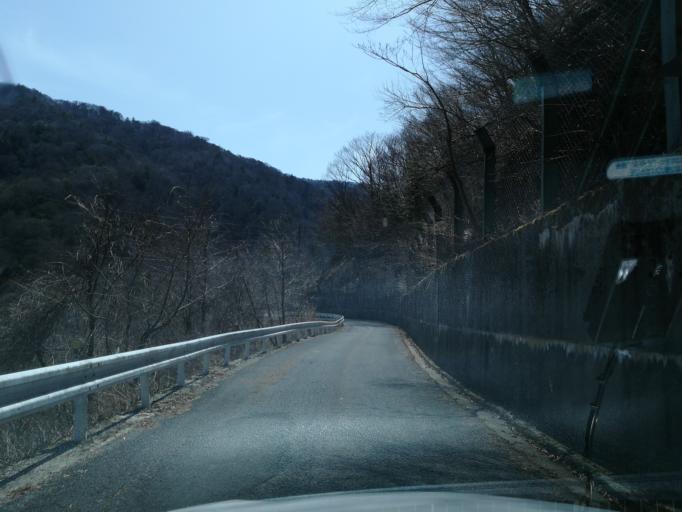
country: JP
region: Tokushima
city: Wakimachi
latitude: 33.8671
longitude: 134.0778
